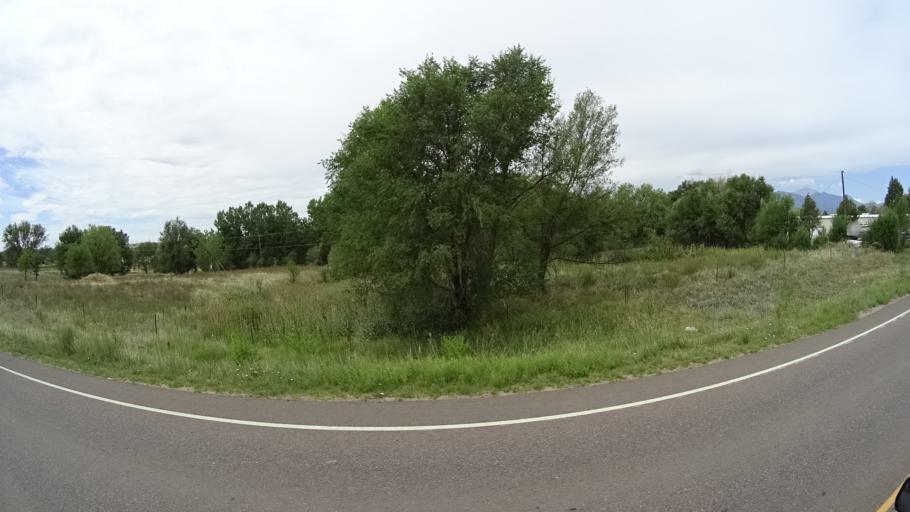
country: US
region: Colorado
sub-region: El Paso County
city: Fountain
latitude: 38.7036
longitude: -104.7092
